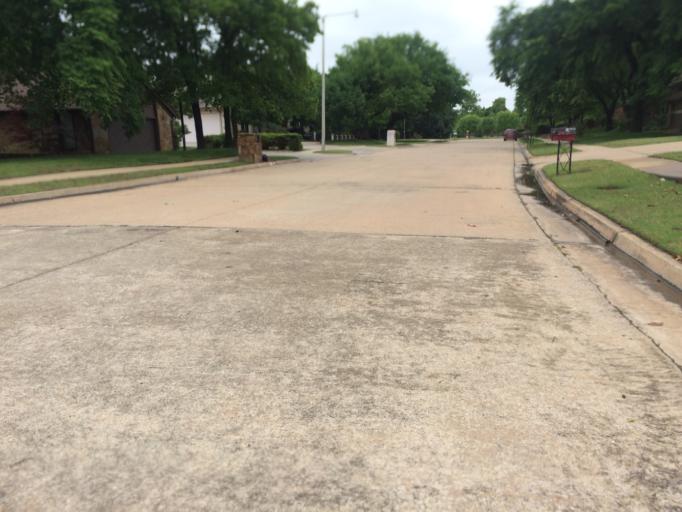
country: US
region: Oklahoma
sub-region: Cleveland County
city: Norman
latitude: 35.1880
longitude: -97.4540
